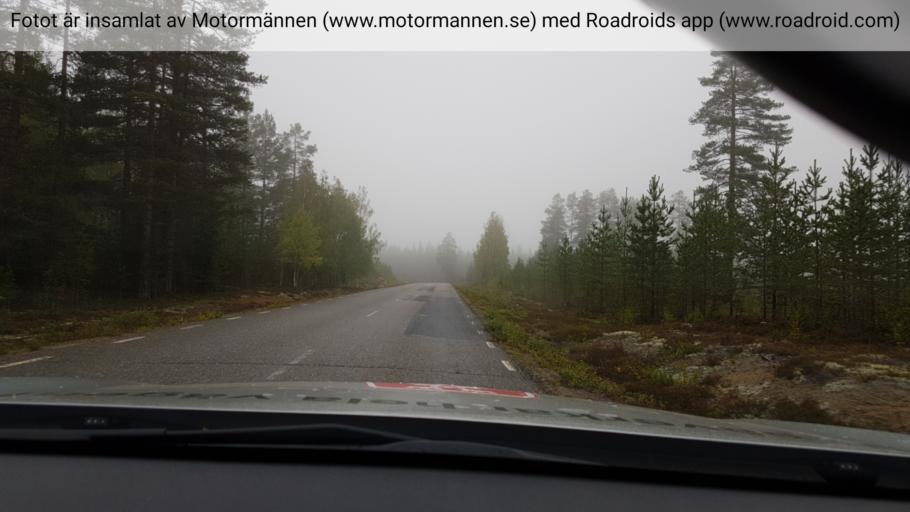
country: SE
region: Vaesterbotten
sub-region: Umea Kommun
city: Ersmark
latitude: 64.2319
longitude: 20.2782
